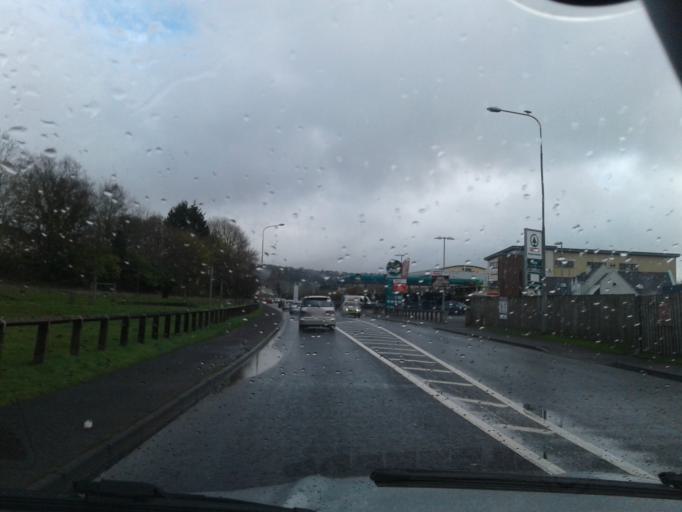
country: IE
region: Ulster
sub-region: County Donegal
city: Letterkenny
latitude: 54.9522
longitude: -7.7106
